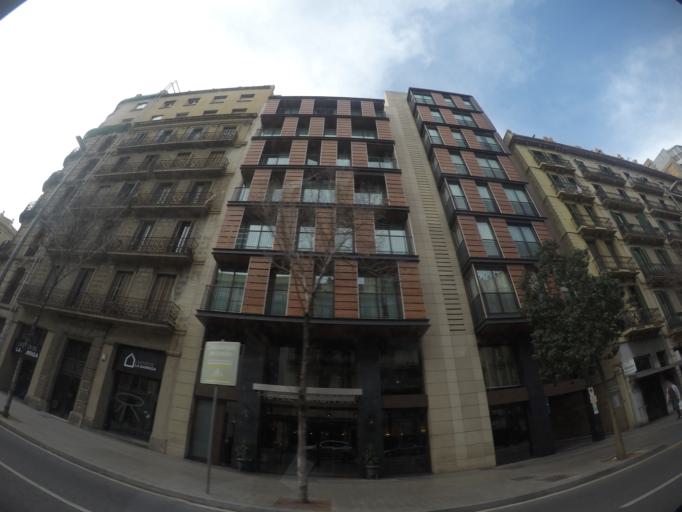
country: ES
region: Catalonia
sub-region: Provincia de Barcelona
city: Eixample
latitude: 41.3963
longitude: 2.1703
